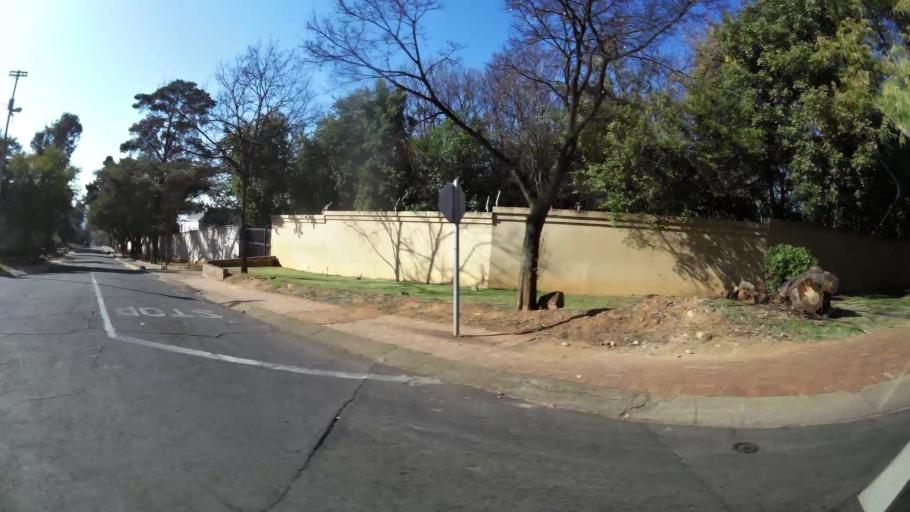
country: ZA
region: Gauteng
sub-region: City of Johannesburg Metropolitan Municipality
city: Midrand
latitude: -26.0585
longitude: 28.0308
